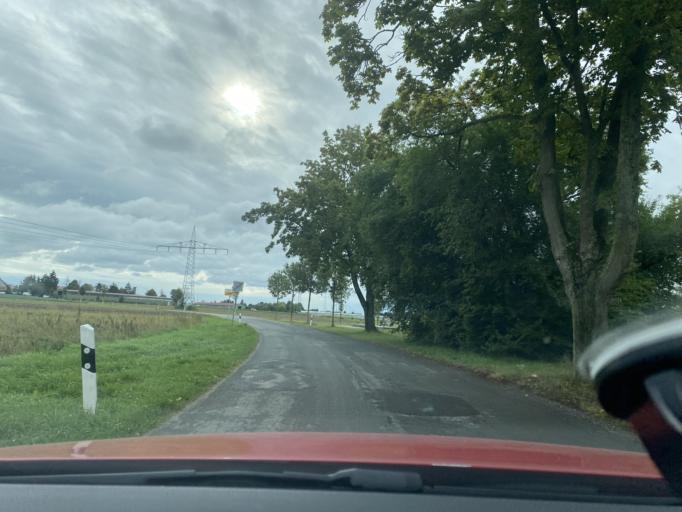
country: DE
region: Bavaria
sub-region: Regierungsbezirk Mittelfranken
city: Furth
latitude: 49.5013
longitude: 11.0027
